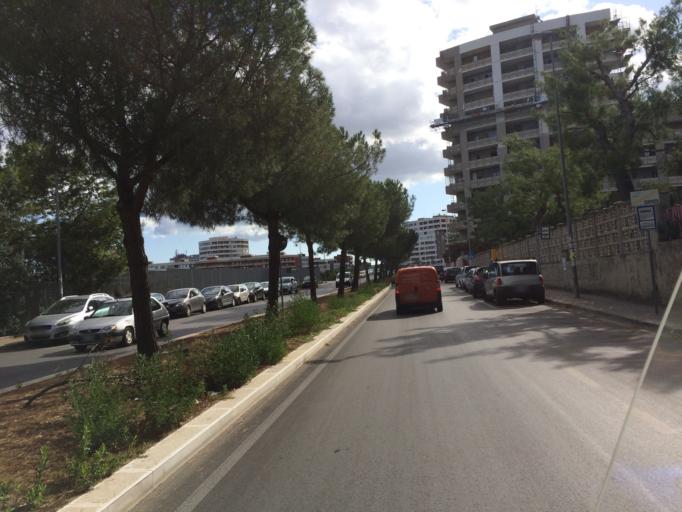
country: IT
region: Apulia
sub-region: Provincia di Bari
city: Bari
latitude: 41.0934
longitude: 16.8548
